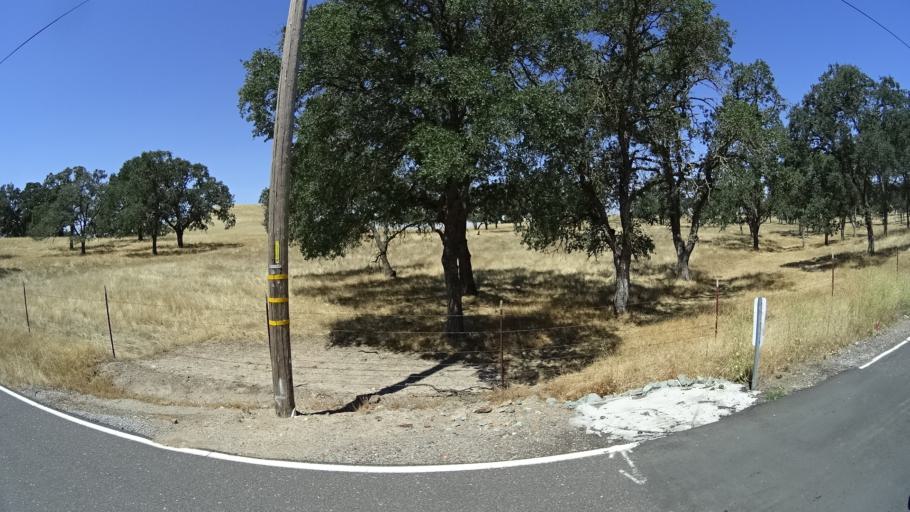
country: US
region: California
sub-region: Calaveras County
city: Rancho Calaveras
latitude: 38.1402
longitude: -120.9448
